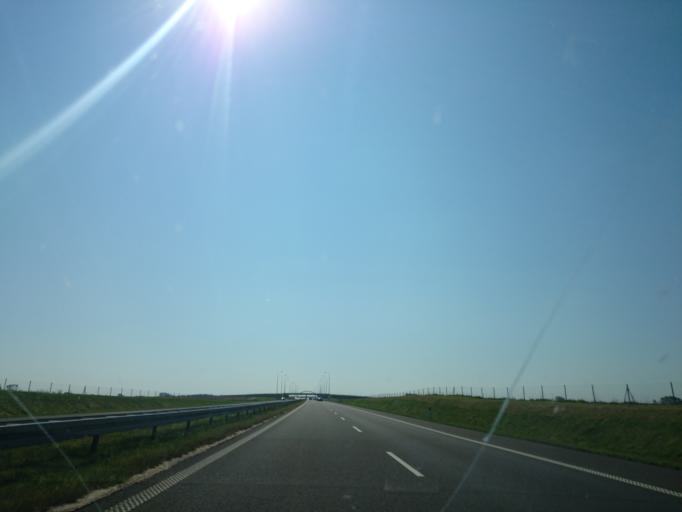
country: PL
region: West Pomeranian Voivodeship
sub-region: Powiat pyrzycki
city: Bielice
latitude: 53.1315
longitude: 14.7280
